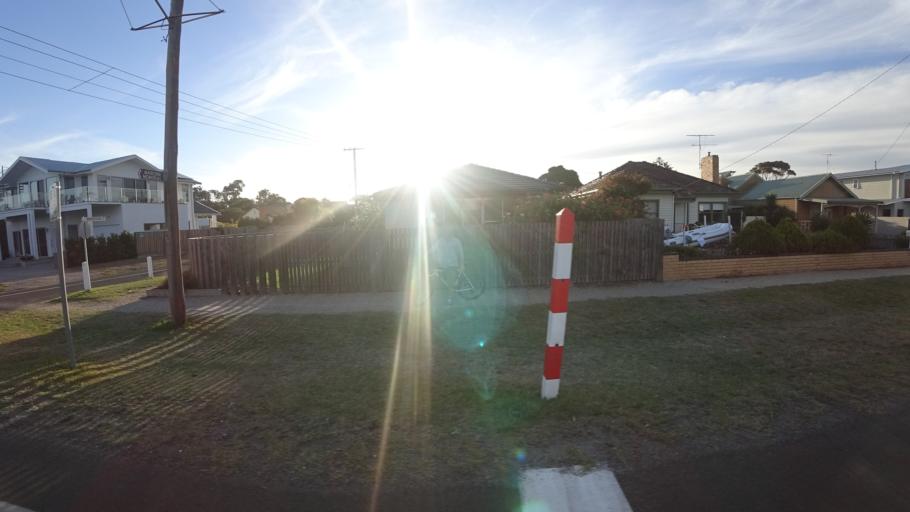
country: AU
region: Victoria
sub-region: Queenscliffe
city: Queenscliff
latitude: -38.2758
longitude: 144.6182
